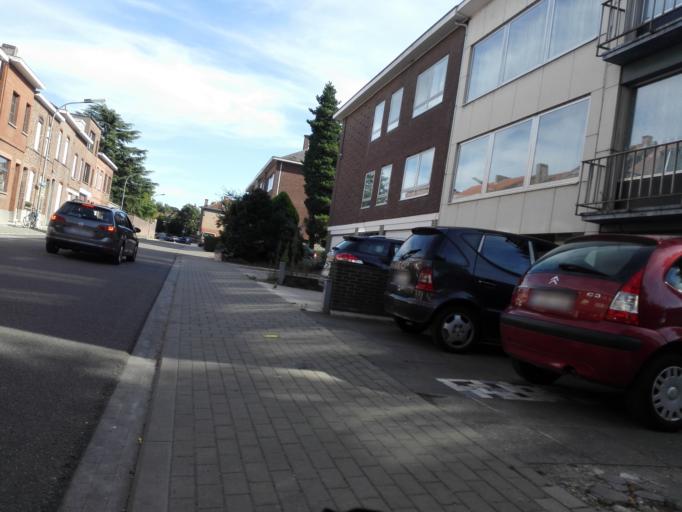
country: BE
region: Flanders
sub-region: Provincie Vlaams-Brabant
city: Leuven
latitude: 50.8907
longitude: 4.7260
